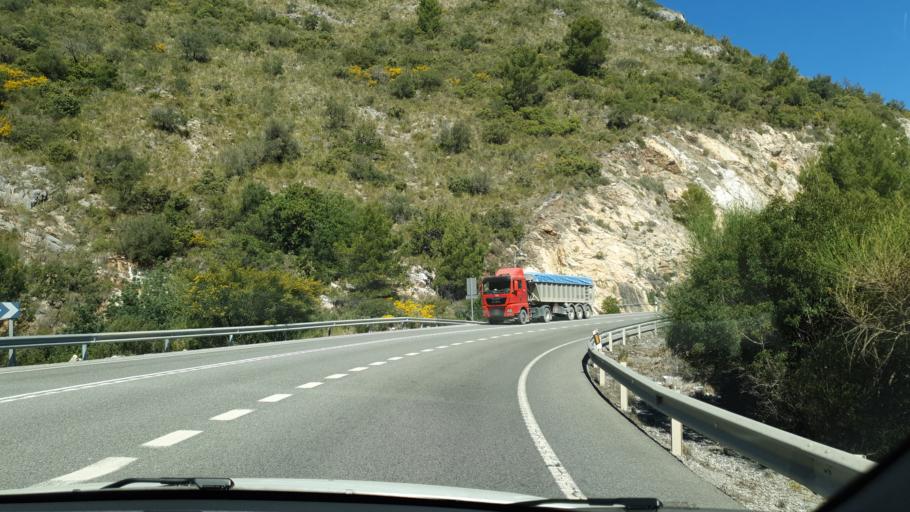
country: ES
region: Andalusia
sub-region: Provincia de Malaga
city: Ojen
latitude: 36.5559
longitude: -4.8652
